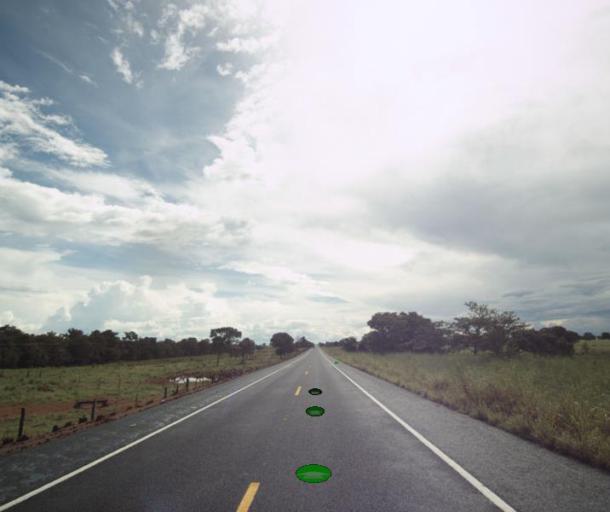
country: BR
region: Goias
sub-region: Sao Miguel Do Araguaia
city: Sao Miguel do Araguaia
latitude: -13.2917
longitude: -50.4086
